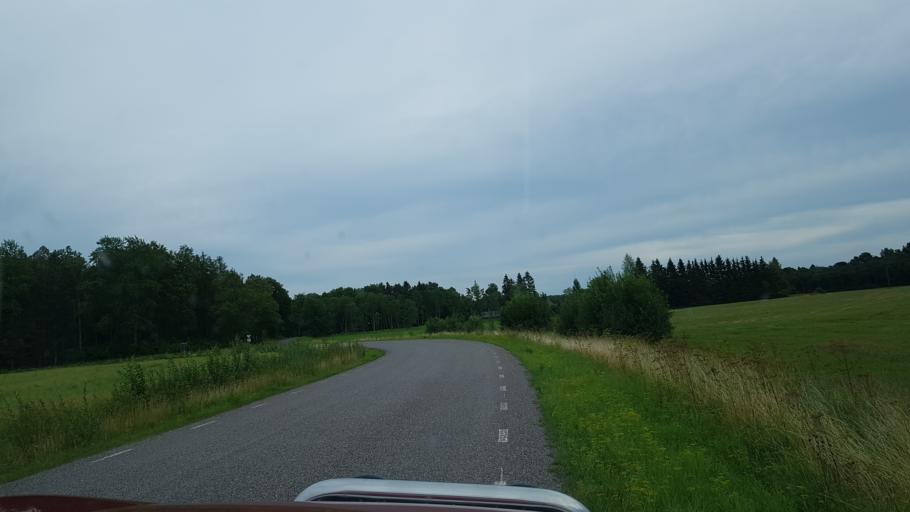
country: EE
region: Laeaene
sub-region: Lihula vald
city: Lihula
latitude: 58.8760
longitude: 23.8034
